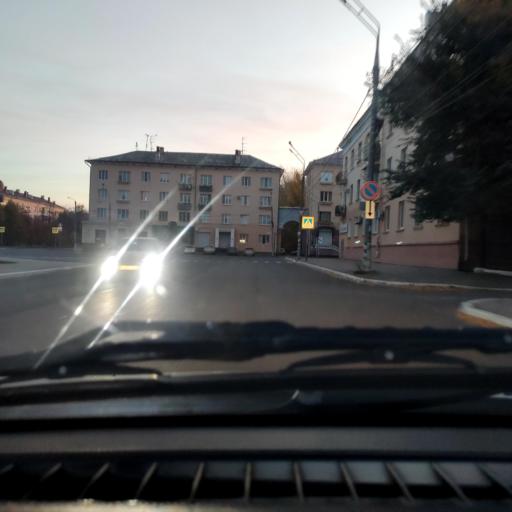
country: RU
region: Samara
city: Tol'yatti
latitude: 53.5132
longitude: 49.4102
